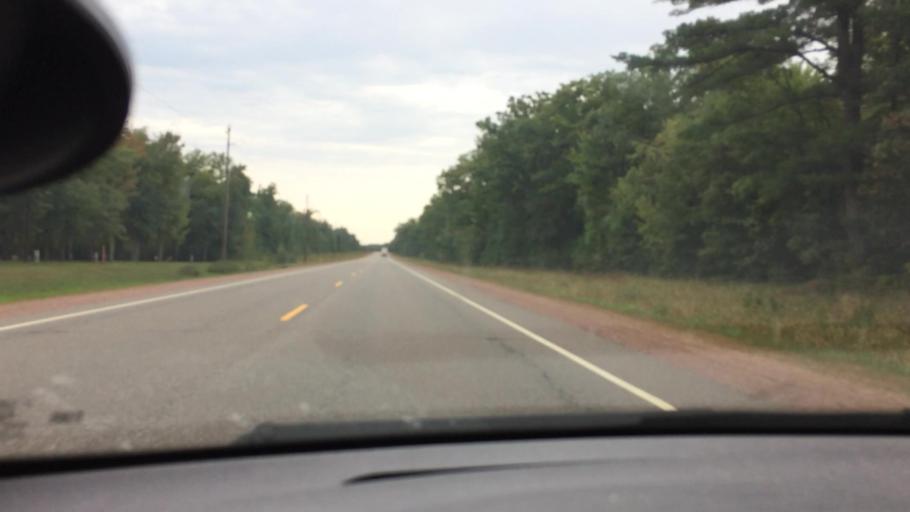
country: US
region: Wisconsin
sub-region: Clark County
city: Neillsville
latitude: 44.5758
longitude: -90.7343
